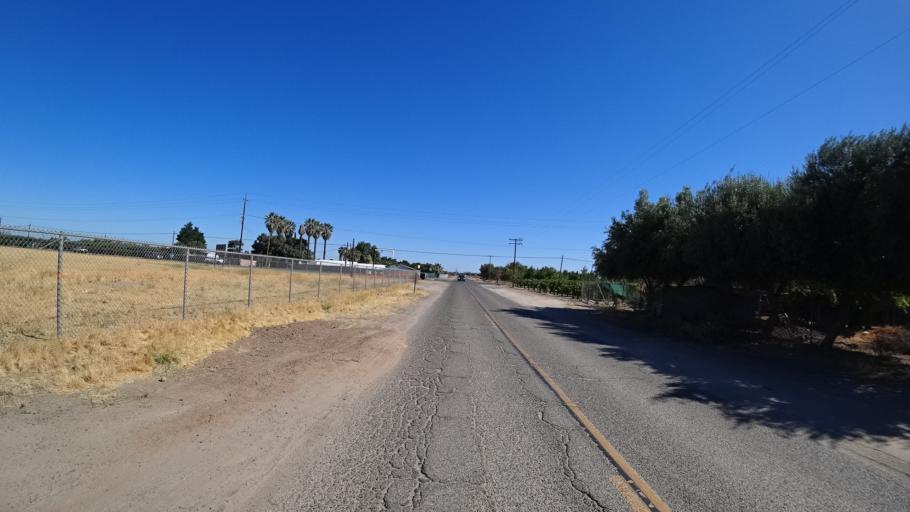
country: US
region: California
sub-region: Fresno County
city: West Park
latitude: 36.7059
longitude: -119.8269
